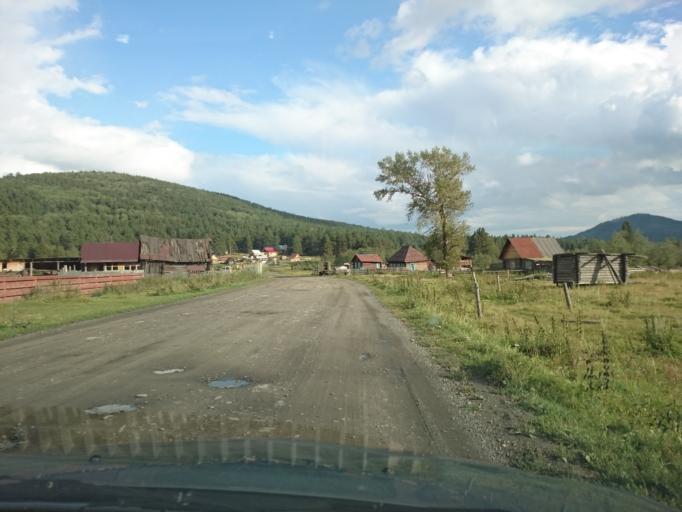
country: RU
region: Bashkortostan
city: Beloretsk
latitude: 54.0480
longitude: 58.3271
